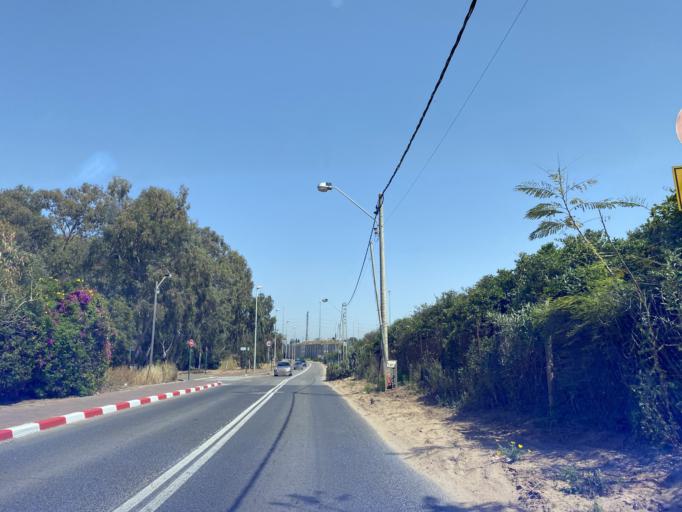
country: IL
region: Central District
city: Ra'anana
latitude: 32.1731
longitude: 34.8764
